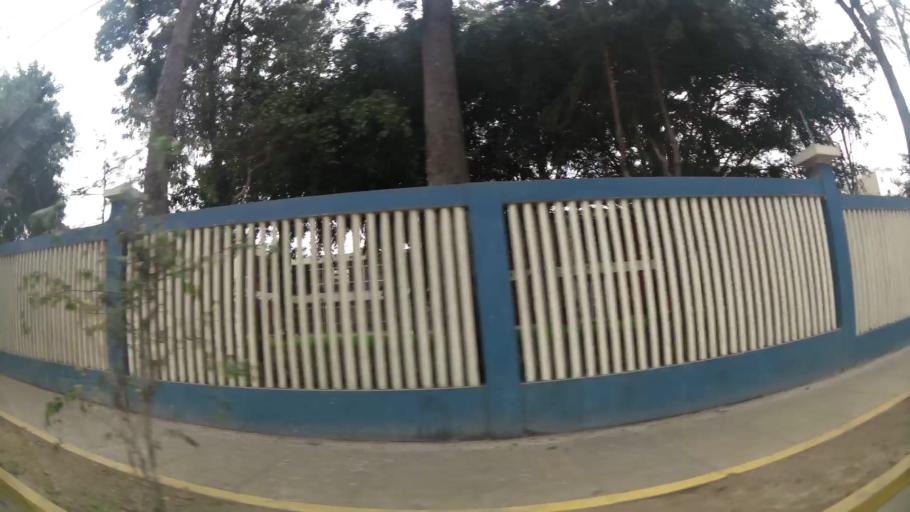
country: PE
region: Lima
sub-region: Lima
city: San Isidro
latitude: -12.0808
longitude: -77.0469
